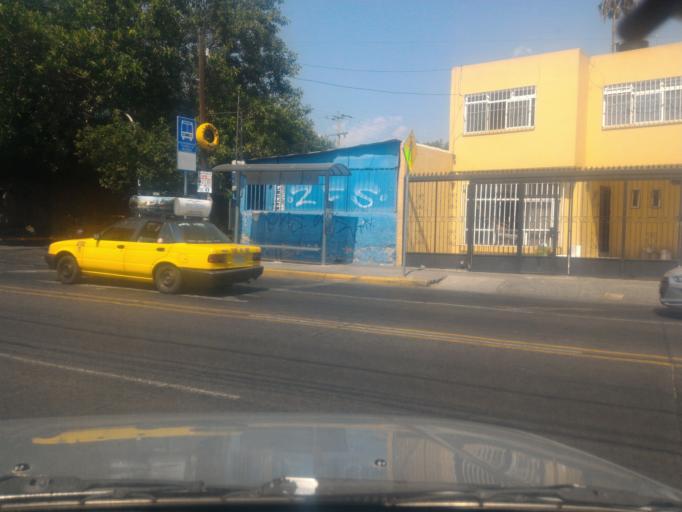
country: MX
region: Jalisco
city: Tlaquepaque
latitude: 20.6902
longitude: -103.3246
